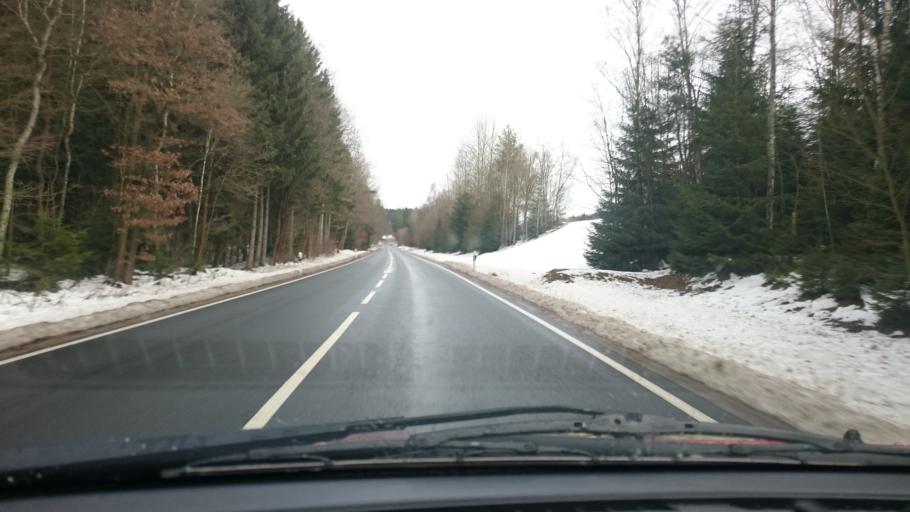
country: DE
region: Saxony
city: Waldkirchen
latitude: 50.5837
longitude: 12.3962
